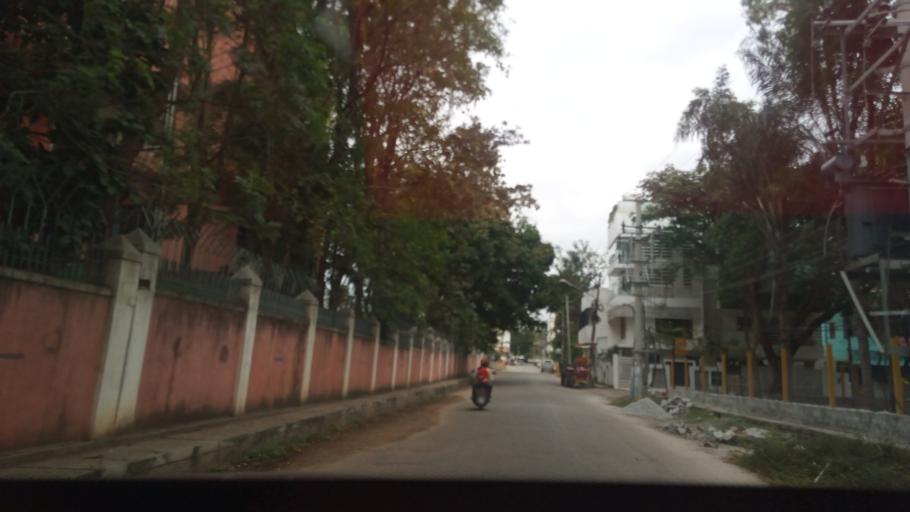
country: IN
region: Karnataka
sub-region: Mysore
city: Mysore
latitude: 12.3022
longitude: 76.6329
